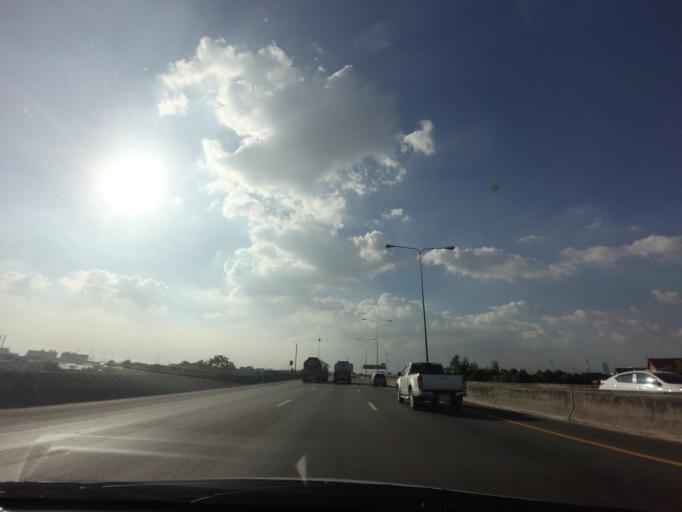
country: TH
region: Samut Prakan
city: Phra Samut Chedi
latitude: 13.6326
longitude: 100.5742
